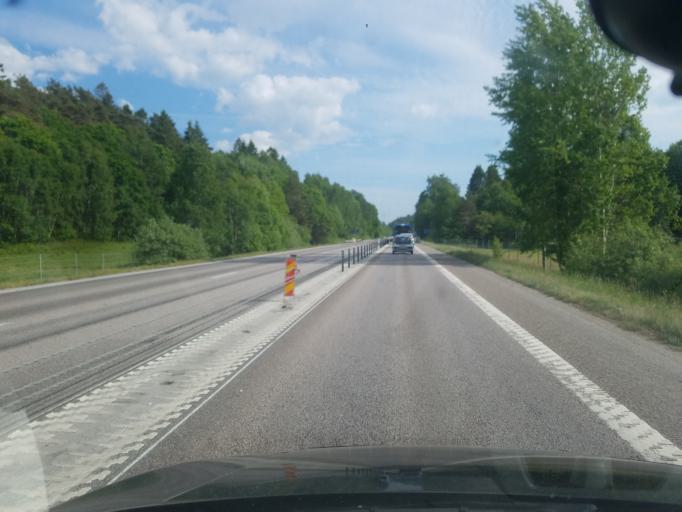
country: SE
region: Vaestra Goetaland
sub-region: Goteborg
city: Billdal
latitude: 57.6053
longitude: 11.9508
